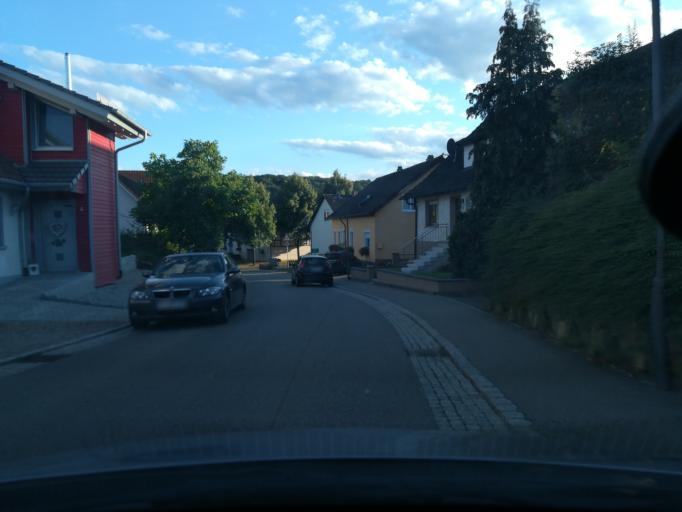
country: DE
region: Baden-Wuerttemberg
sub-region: Freiburg Region
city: Moos
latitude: 47.7392
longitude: 8.8972
